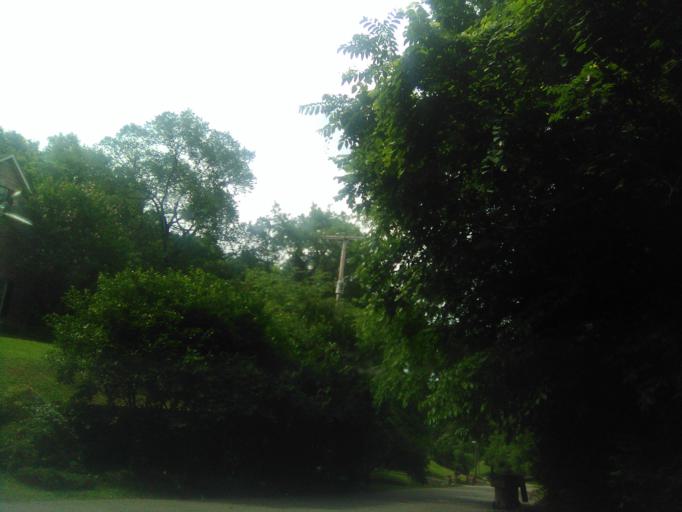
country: US
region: Tennessee
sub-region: Davidson County
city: Belle Meade
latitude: 36.0954
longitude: -86.8959
